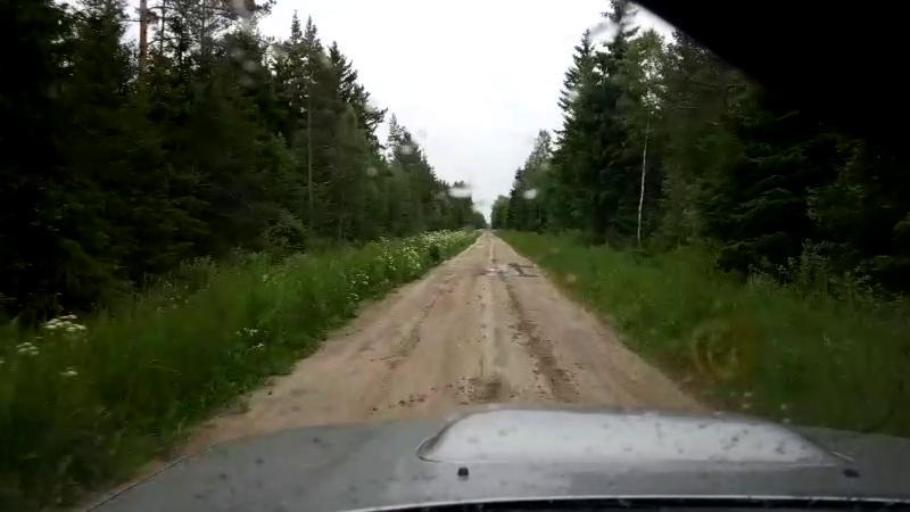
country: EE
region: Paernumaa
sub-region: Halinga vald
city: Parnu-Jaagupi
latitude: 58.5867
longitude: 24.6346
